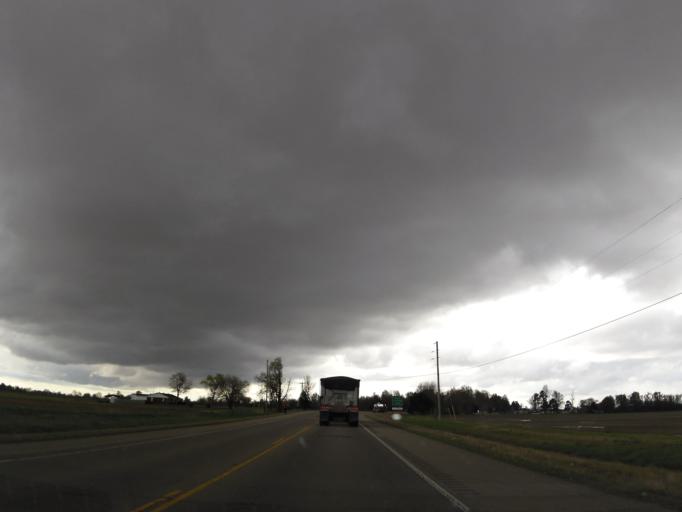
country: US
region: Arkansas
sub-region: Clay County
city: Corning
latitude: 36.4931
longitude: -90.5400
